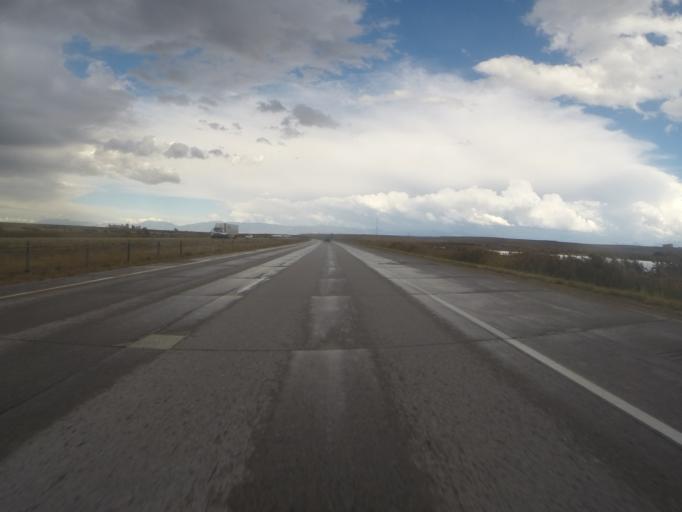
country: US
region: Utah
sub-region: Salt Lake County
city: Magna
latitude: 40.7378
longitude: -112.1931
